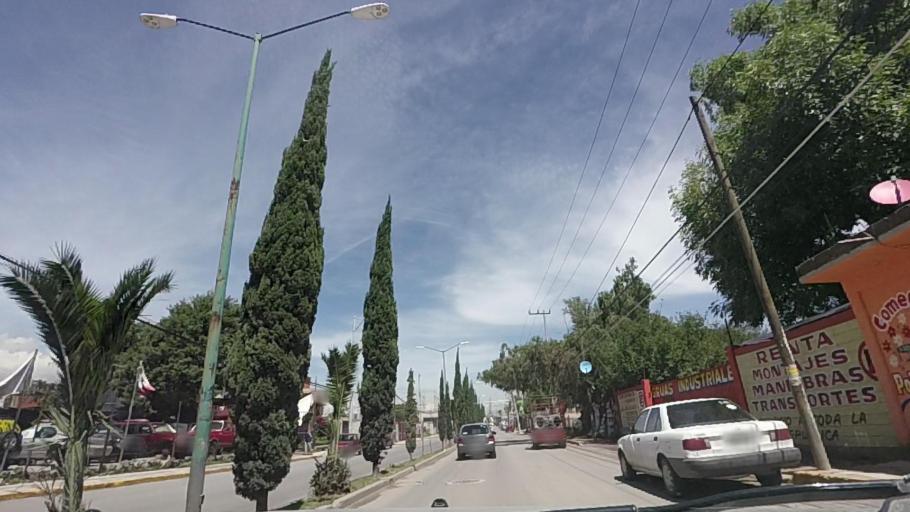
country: MX
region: Mexico
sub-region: Huehuetoca
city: Casa Nueva
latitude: 19.8306
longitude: -99.2207
